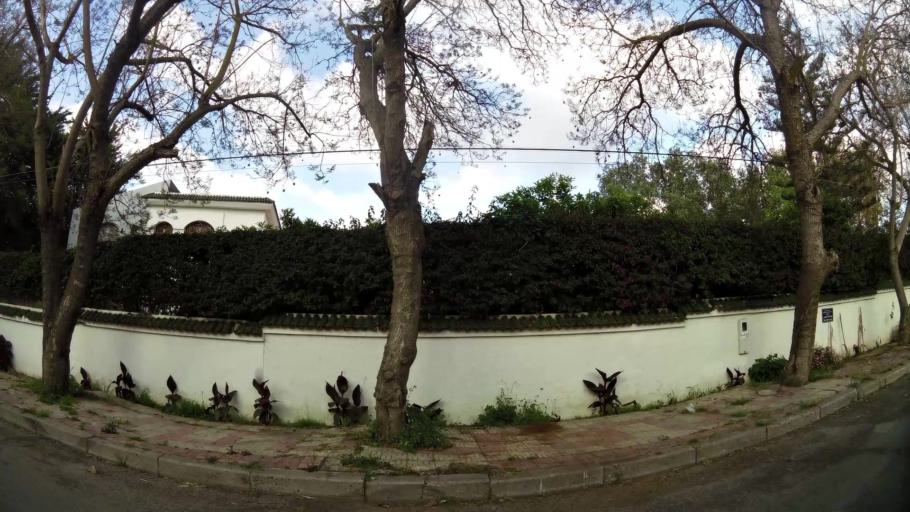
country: MA
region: Rabat-Sale-Zemmour-Zaer
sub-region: Rabat
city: Rabat
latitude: 33.9578
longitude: -6.8339
